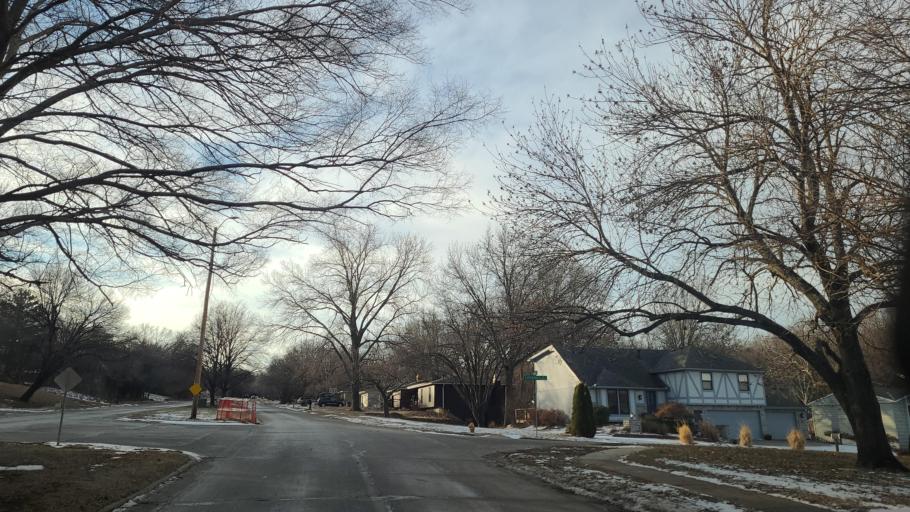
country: US
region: Kansas
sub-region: Douglas County
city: Lawrence
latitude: 38.9798
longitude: -95.2717
